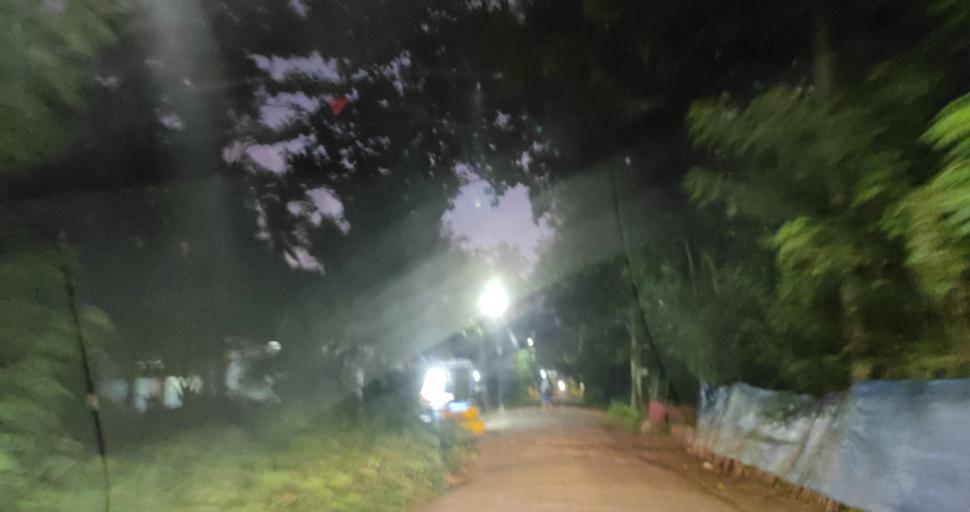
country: IN
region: Kerala
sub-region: Alappuzha
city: Shertallai
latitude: 9.6231
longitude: 76.3513
